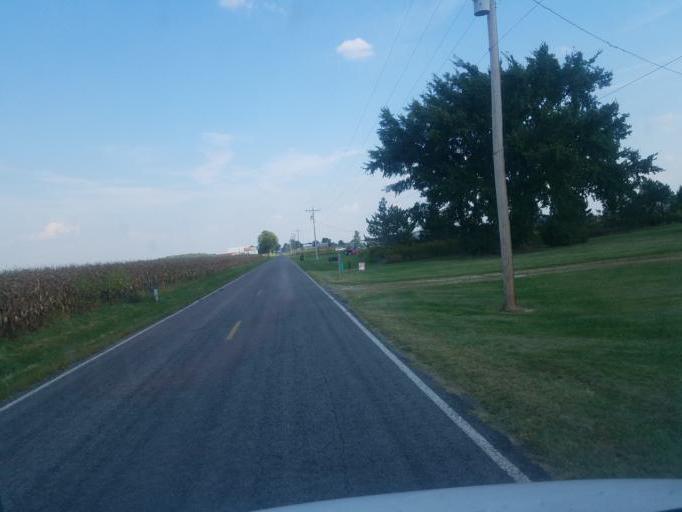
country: US
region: Ohio
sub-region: Hardin County
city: Forest
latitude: 40.9049
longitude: -83.4987
